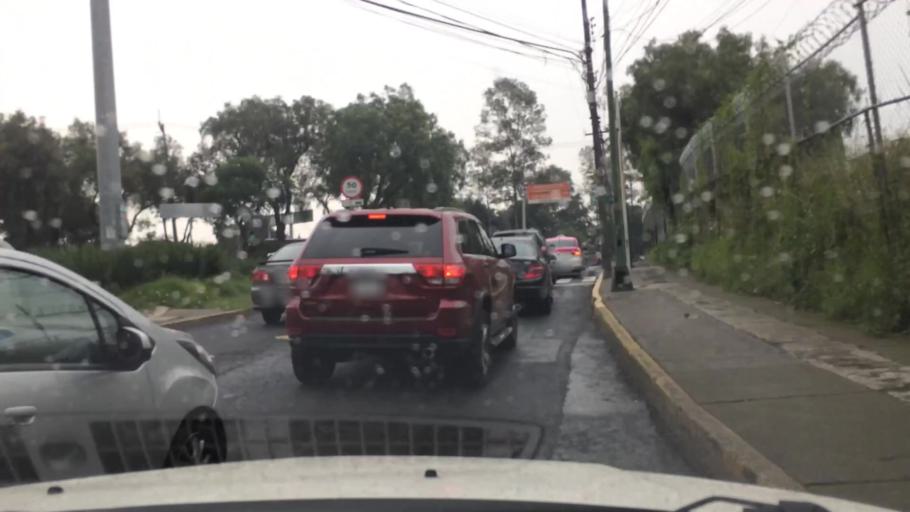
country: MX
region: Mexico City
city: Magdalena Contreras
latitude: 19.3068
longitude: -99.2055
